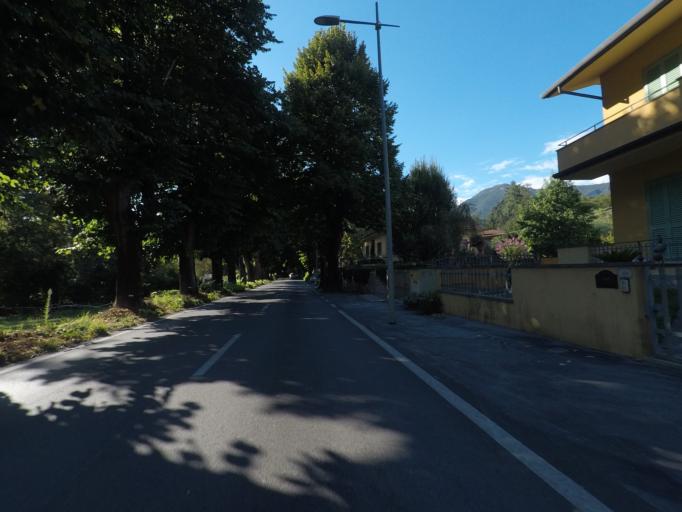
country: IT
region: Tuscany
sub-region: Provincia di Lucca
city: Corsanico-Bargecchia
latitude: 43.9265
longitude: 10.3208
